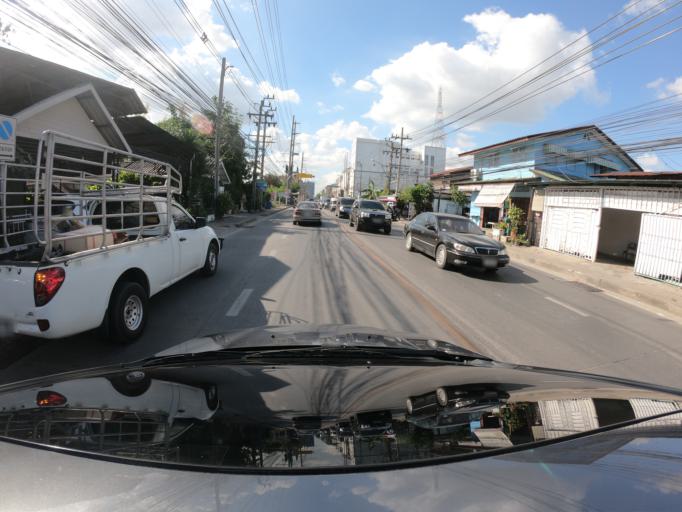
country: TH
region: Bangkok
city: Bang Na
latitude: 13.6524
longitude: 100.6171
